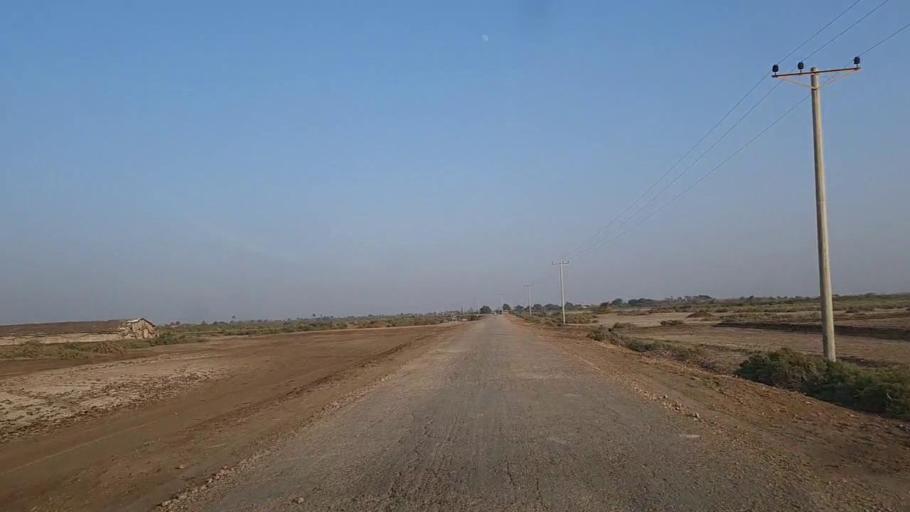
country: PK
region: Sindh
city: Keti Bandar
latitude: 24.2794
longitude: 67.6329
